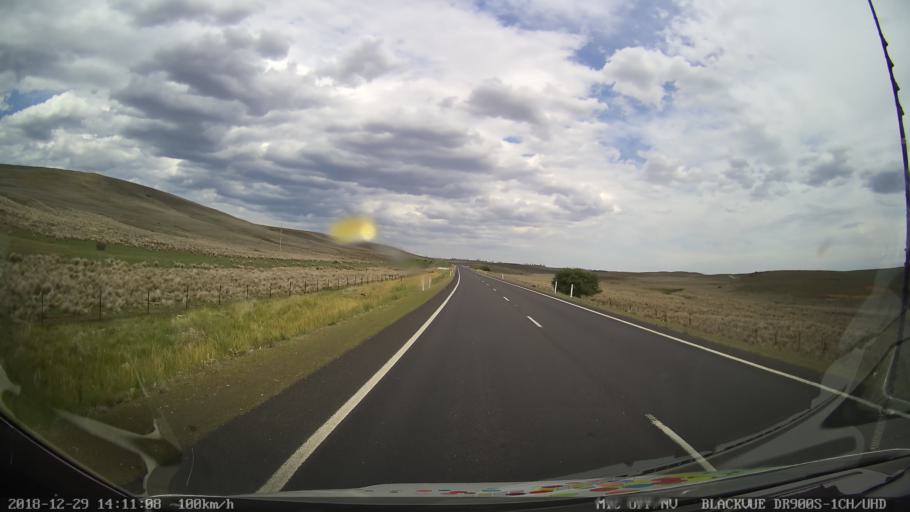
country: AU
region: New South Wales
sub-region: Cooma-Monaro
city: Cooma
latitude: -36.4015
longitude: 149.2183
